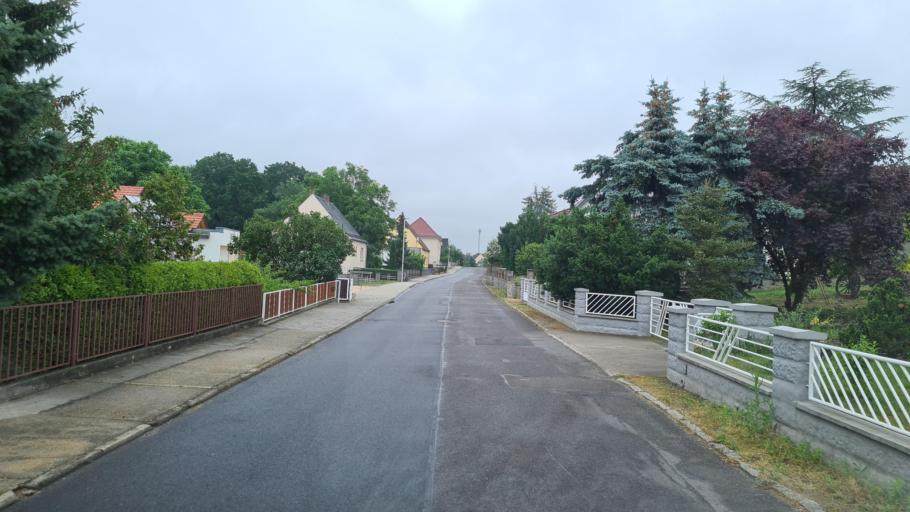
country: DE
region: Brandenburg
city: Ortrand
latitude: 51.3730
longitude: 13.7502
